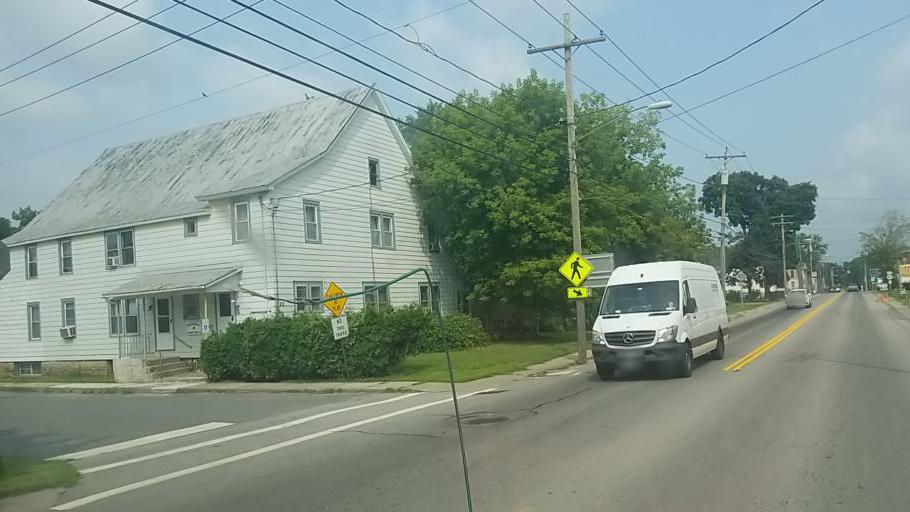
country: US
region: New York
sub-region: Montgomery County
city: Fort Plain
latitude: 42.9328
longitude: -74.6125
